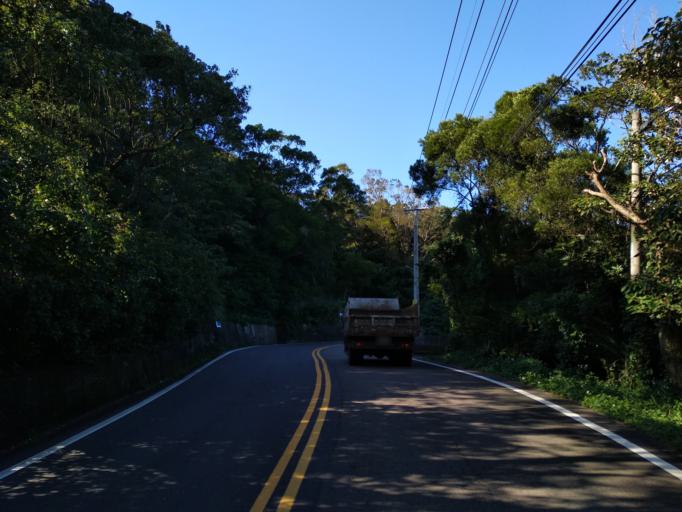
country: TW
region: Taiwan
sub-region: Hsinchu
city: Zhubei
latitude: 24.8603
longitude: 121.0955
